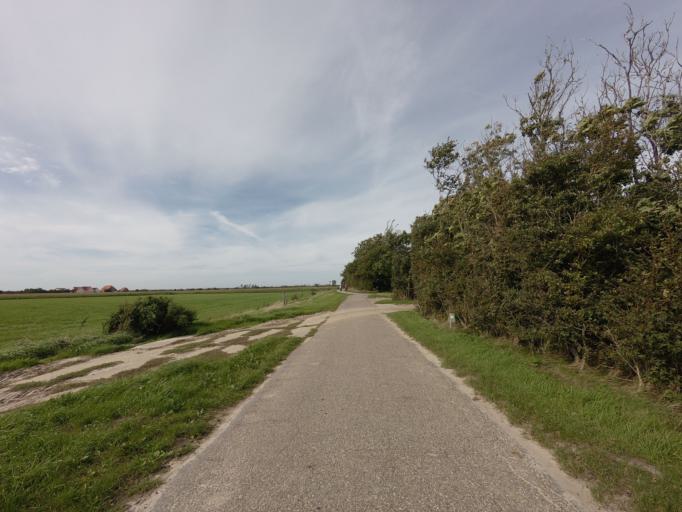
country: NL
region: North Holland
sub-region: Gemeente Texel
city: Den Burg
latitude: 53.0720
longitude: 4.8115
